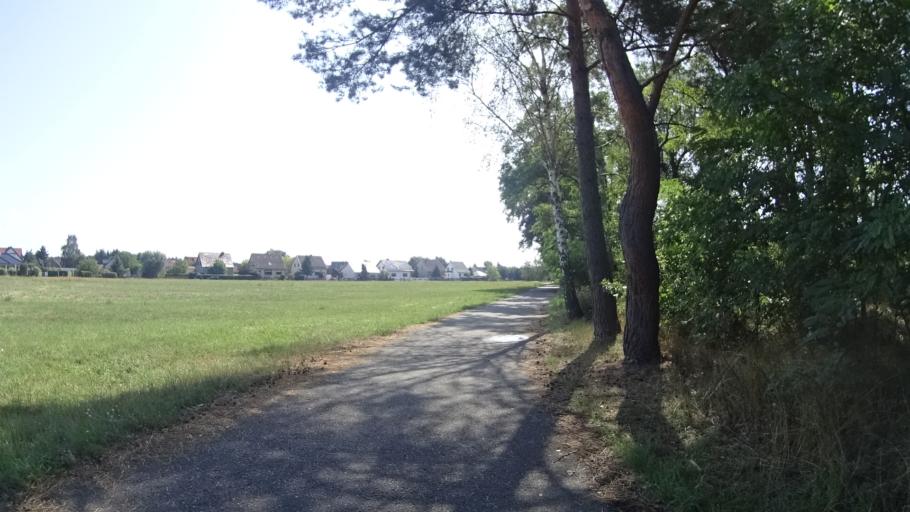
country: DE
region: Brandenburg
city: Cottbus
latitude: 51.7943
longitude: 14.3004
